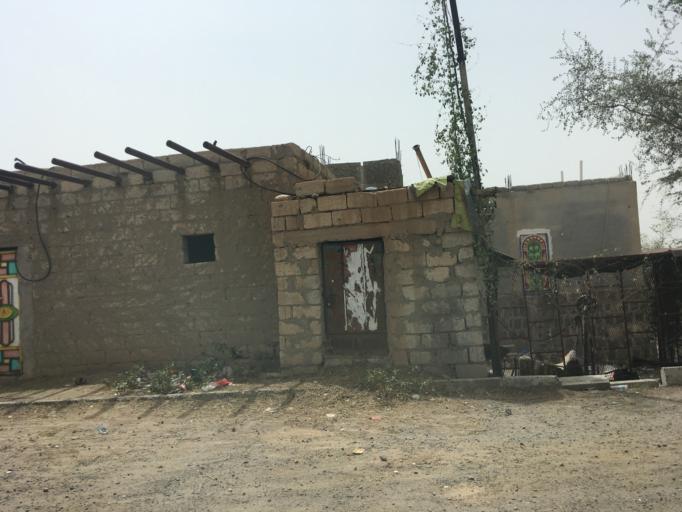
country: YE
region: Ad Dali'
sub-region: Qa'atabah
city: Qa`tabah
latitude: 13.8298
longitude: 44.7267
